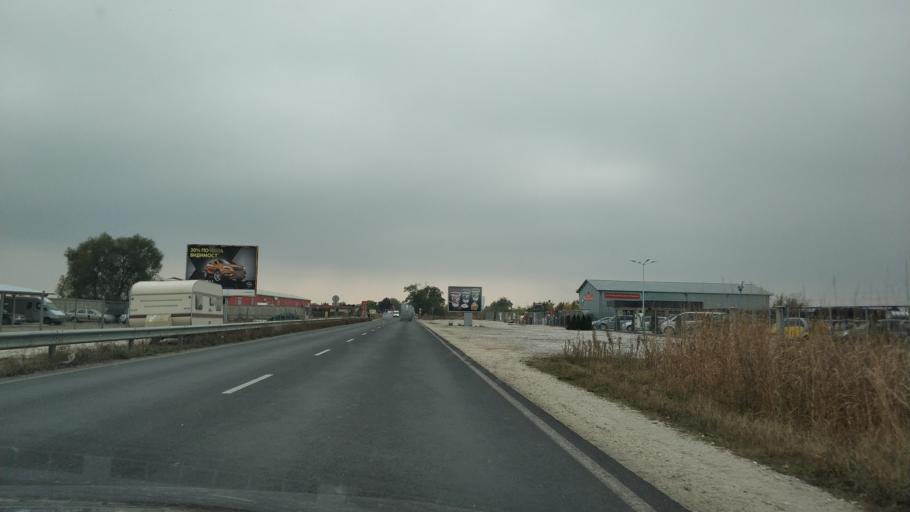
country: BG
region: Plovdiv
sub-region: Obshtina Plovdiv
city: Plovdiv
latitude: 42.2436
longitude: 24.7235
